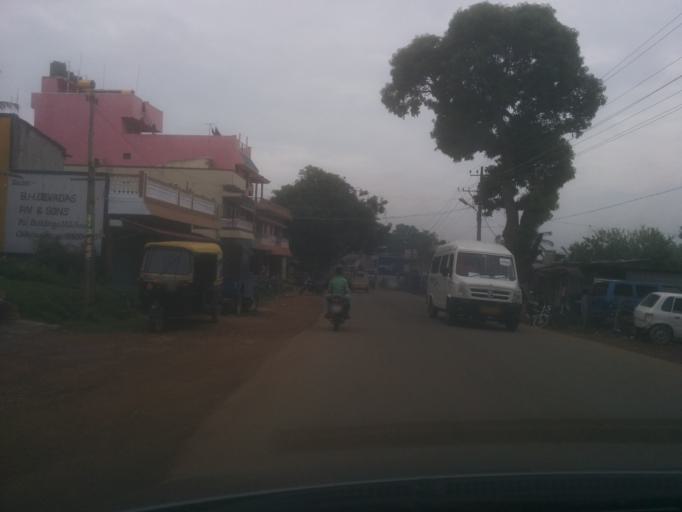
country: IN
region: Karnataka
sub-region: Chikmagalur
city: Chikmagalur
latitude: 13.3383
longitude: 75.7696
